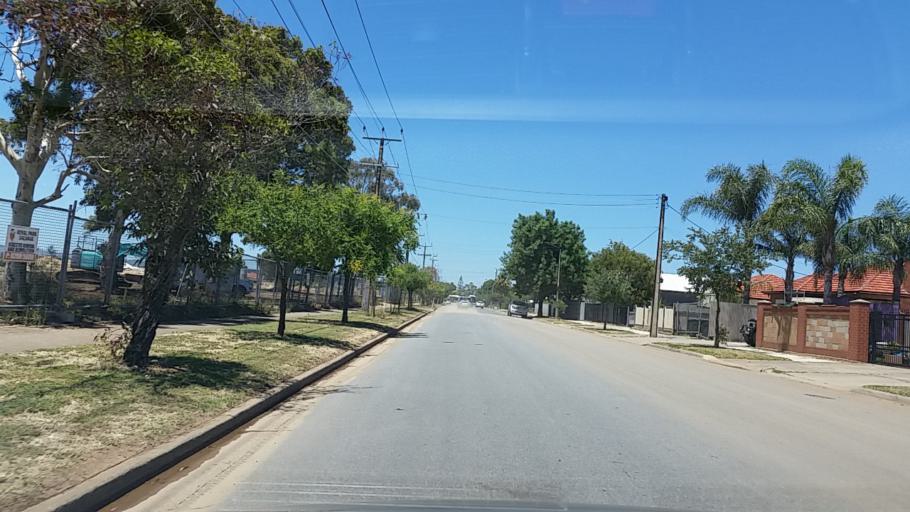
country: AU
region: South Australia
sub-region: Charles Sturt
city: Woodville
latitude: -34.8771
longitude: 138.5574
